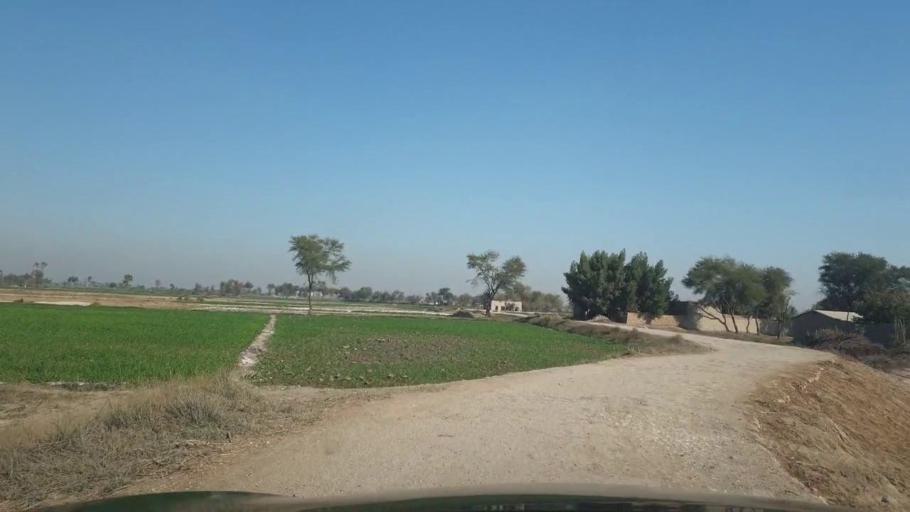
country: PK
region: Sindh
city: Ghotki
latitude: 27.9987
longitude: 69.3564
